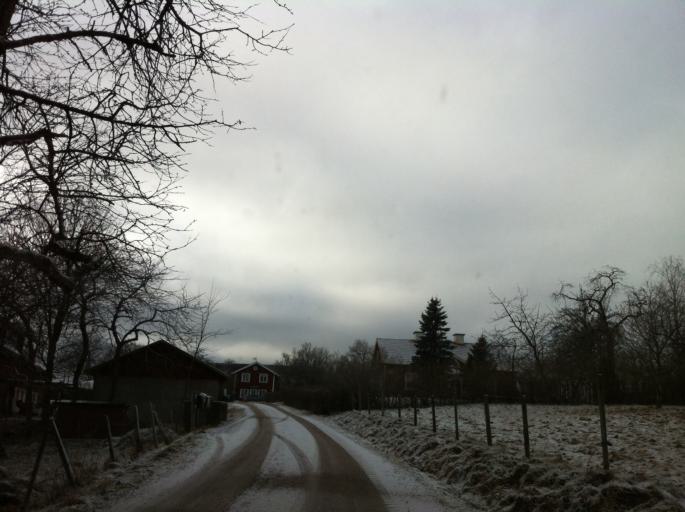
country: SE
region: Joenkoeping
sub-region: Eksjo Kommun
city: Mariannelund
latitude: 57.6130
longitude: 15.7054
